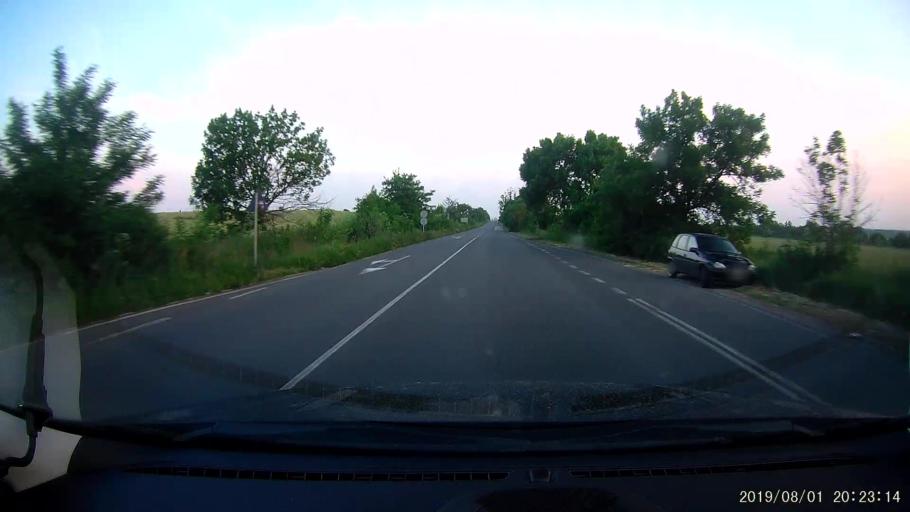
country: BG
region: Yambol
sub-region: Obshtina Elkhovo
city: Elkhovo
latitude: 42.2527
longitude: 26.5988
